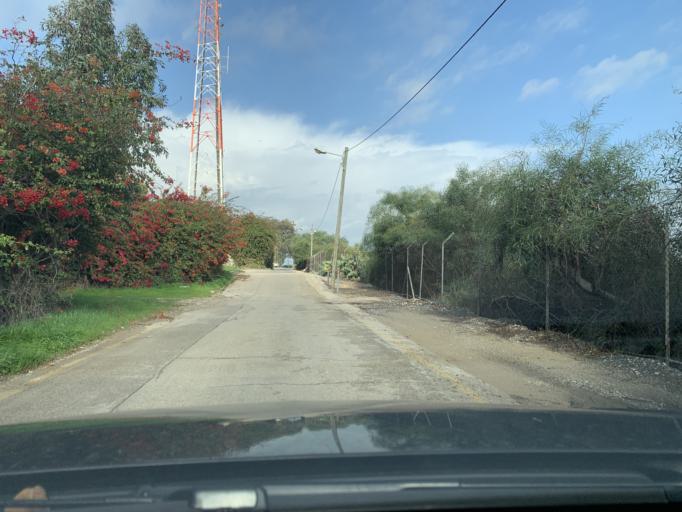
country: PS
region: West Bank
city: Qalqilyah
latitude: 32.1951
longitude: 34.9526
